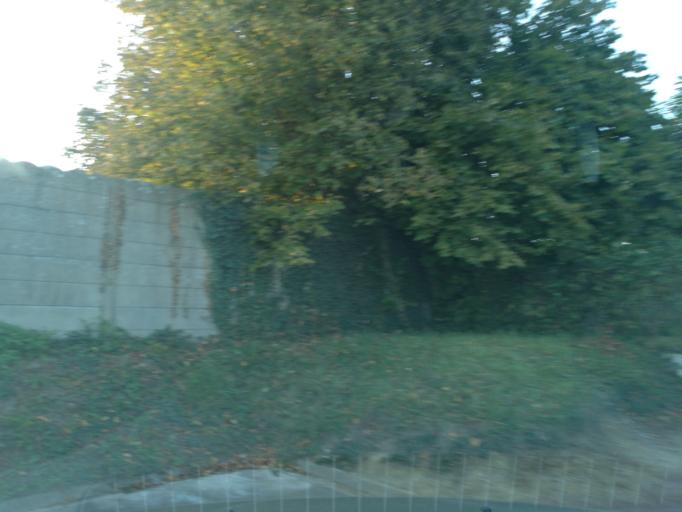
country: FR
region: Brittany
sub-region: Departement d'Ille-et-Vilaine
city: Pleumeleuc
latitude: 48.1833
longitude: -1.9181
